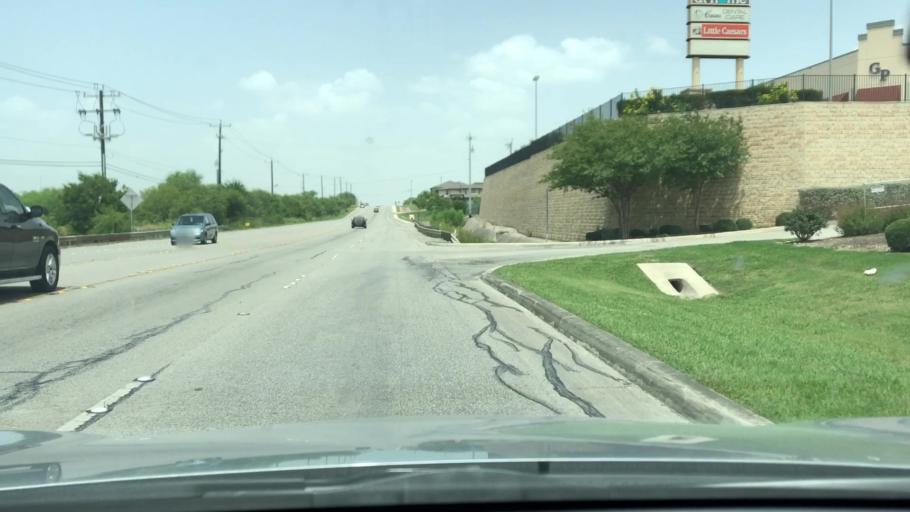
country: US
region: Texas
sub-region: Bexar County
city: Live Oak
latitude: 29.5791
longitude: -98.3415
